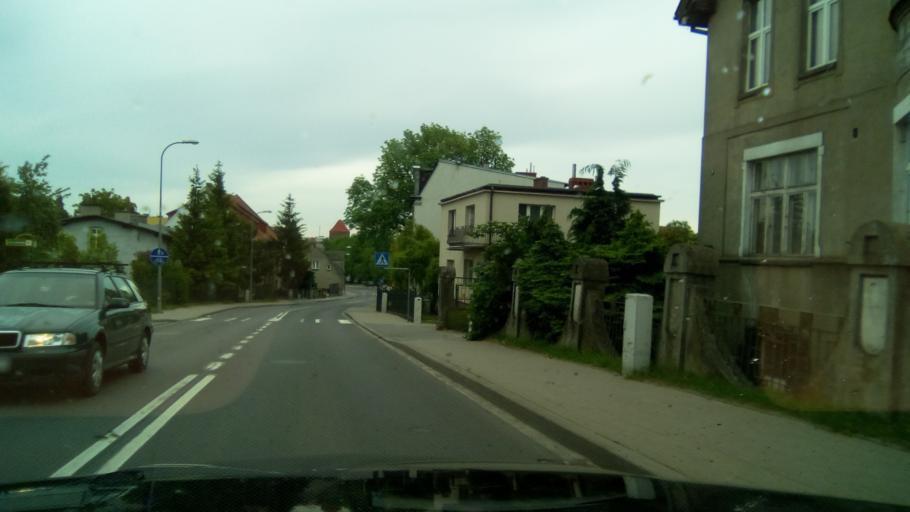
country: PL
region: Pomeranian Voivodeship
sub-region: Powiat chojnicki
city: Chojnice
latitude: 53.6920
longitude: 17.5543
